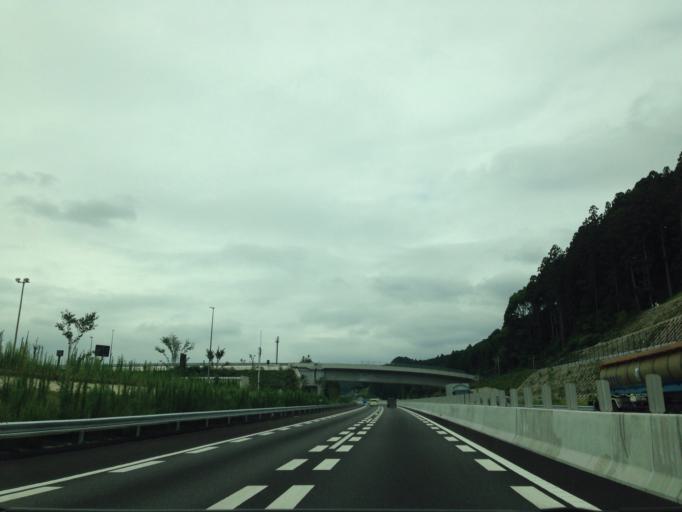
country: JP
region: Aichi
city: Shinshiro
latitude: 34.9251
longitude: 137.5067
